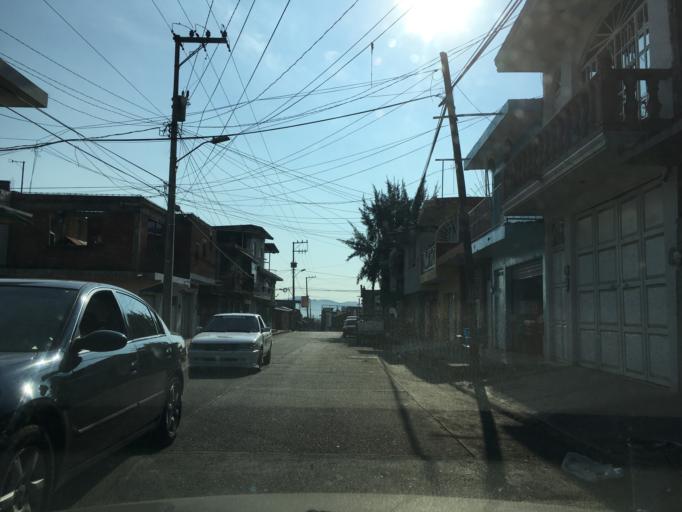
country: MX
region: Michoacan
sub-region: Uruapan
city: Uruapan
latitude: 19.4077
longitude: -102.0721
